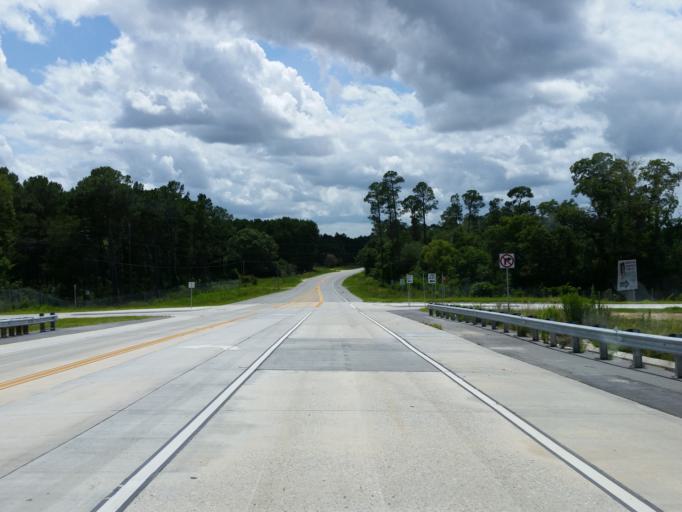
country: US
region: Georgia
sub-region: Tift County
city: Unionville
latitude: 31.3584
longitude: -83.4910
